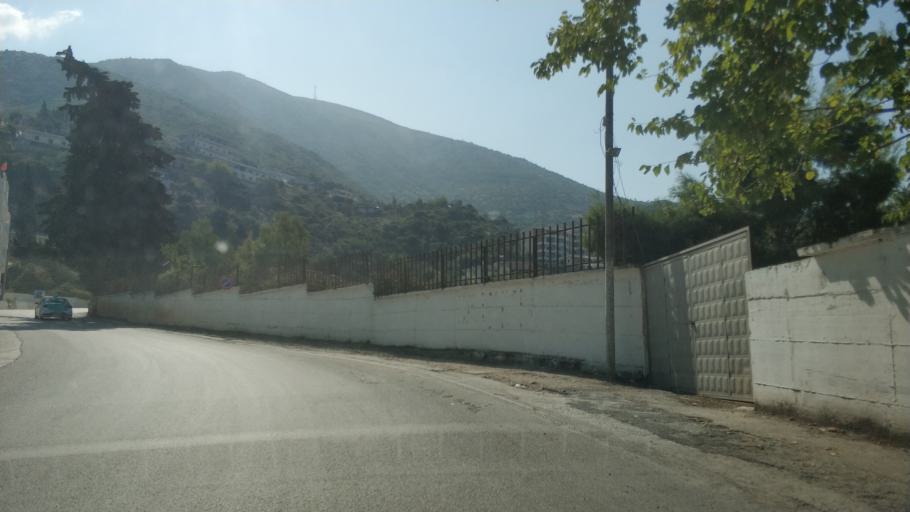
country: AL
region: Vlore
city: Vlore
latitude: 40.4188
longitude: 19.4866
